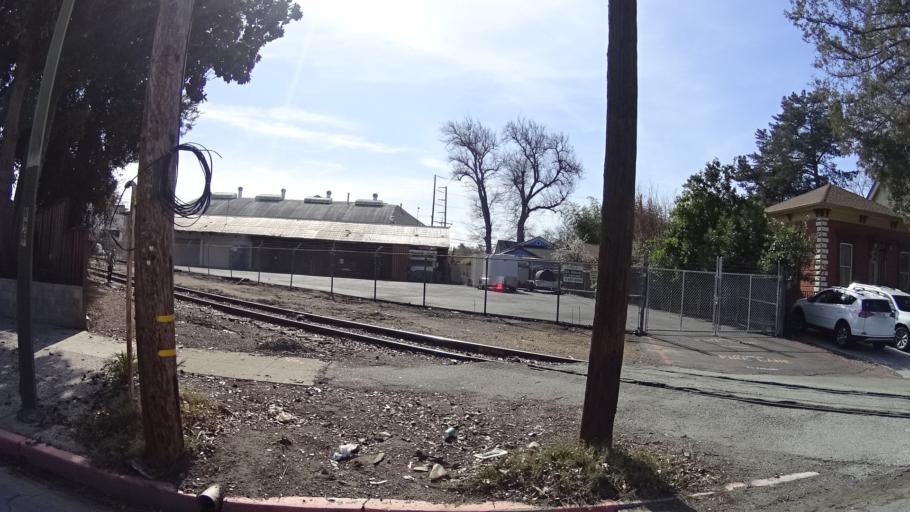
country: US
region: California
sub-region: Santa Clara County
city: San Jose
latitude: 37.3456
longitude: -121.8920
